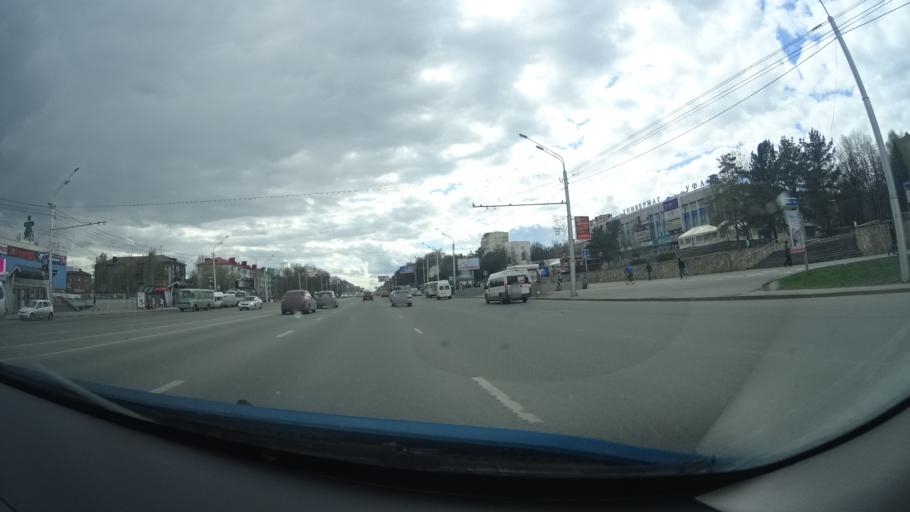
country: RU
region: Bashkortostan
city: Ufa
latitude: 54.7510
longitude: 55.9989
